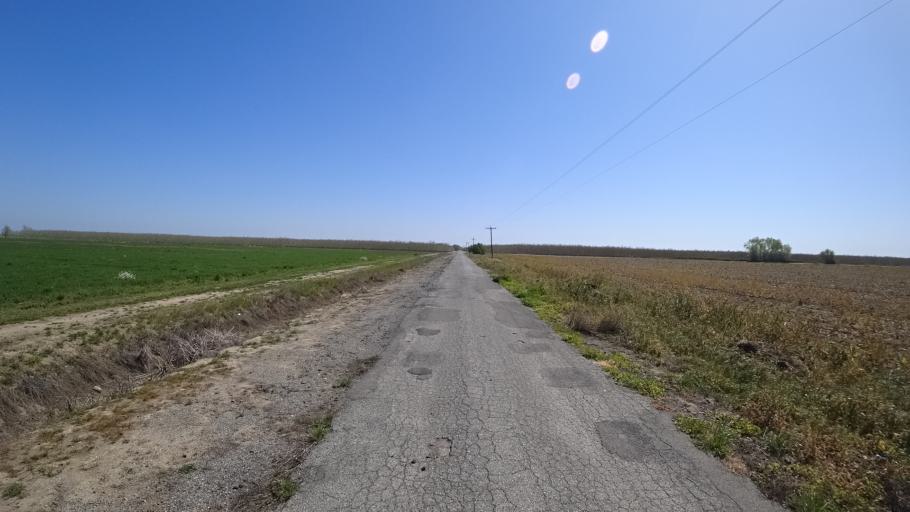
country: US
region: California
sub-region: Glenn County
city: Willows
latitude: 39.4990
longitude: -122.0355
